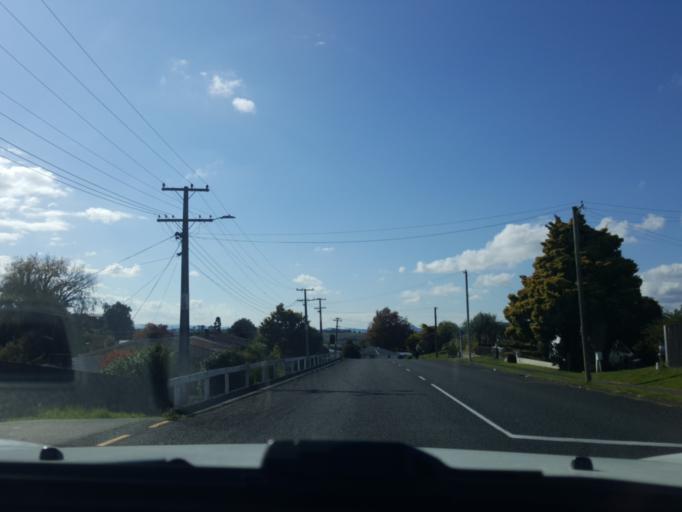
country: NZ
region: Waikato
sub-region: Waikato District
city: Ngaruawahia
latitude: -37.5432
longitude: 175.1700
